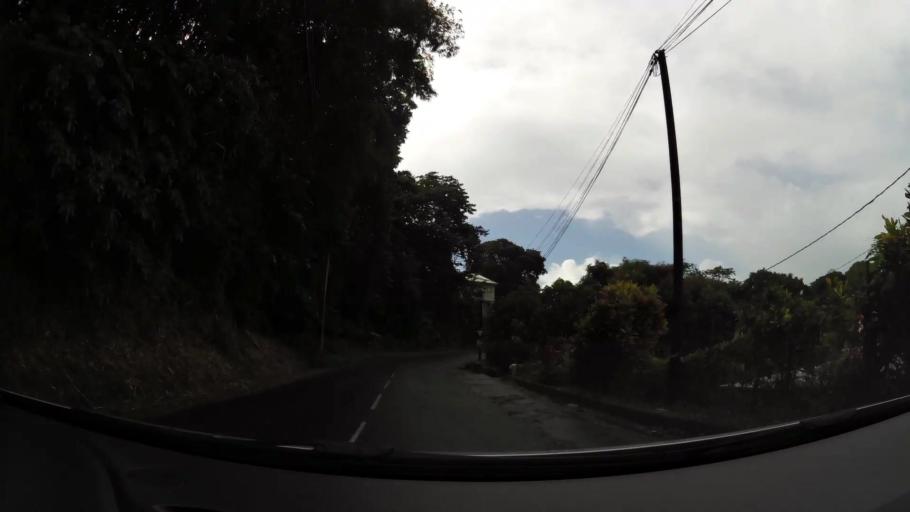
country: MQ
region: Martinique
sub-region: Martinique
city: Saint-Joseph
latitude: 14.6538
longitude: -61.0379
